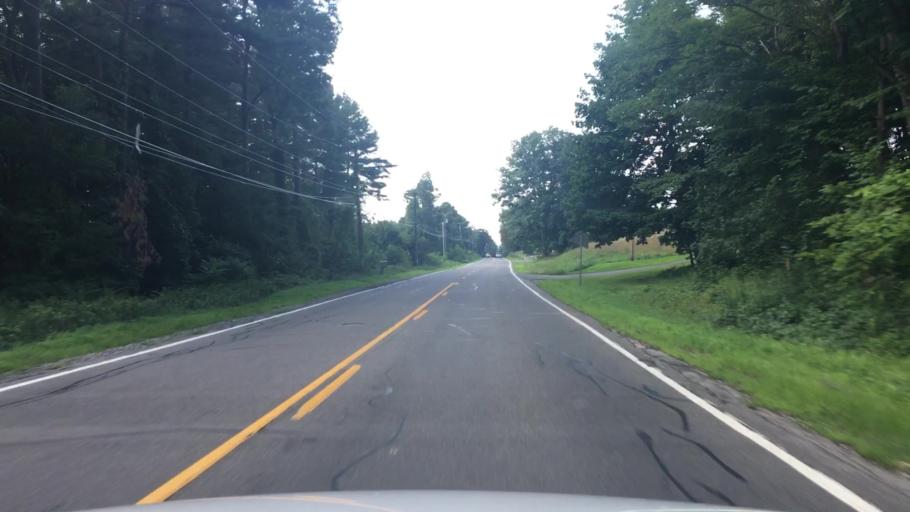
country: US
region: New Hampshire
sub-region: Rockingham County
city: Auburn
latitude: 42.9697
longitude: -71.3649
